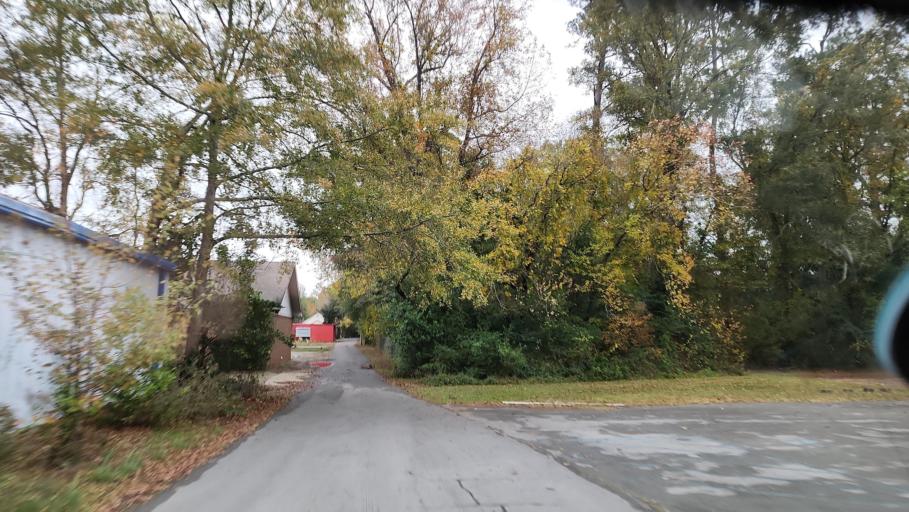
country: US
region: Mississippi
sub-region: Forrest County
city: Hattiesburg
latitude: 31.3242
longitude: -89.3055
